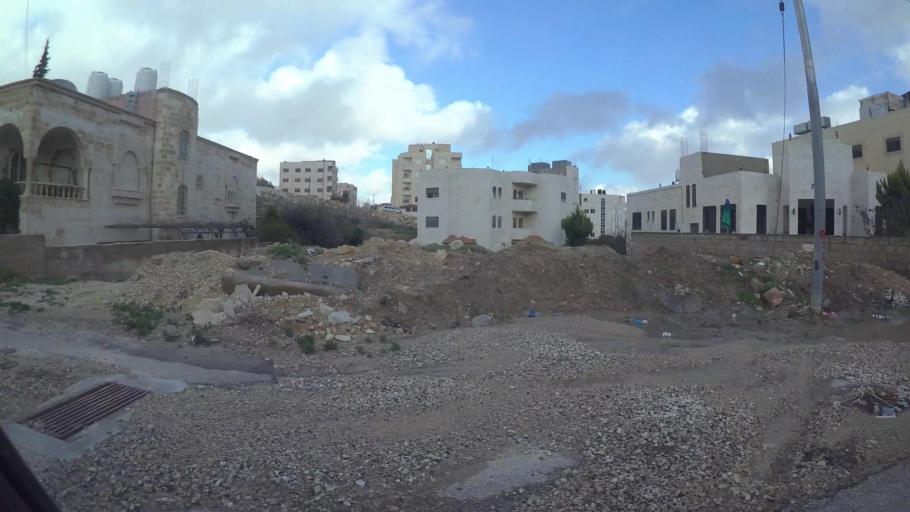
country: JO
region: Amman
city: Al Jubayhah
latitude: 32.0532
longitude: 35.8917
